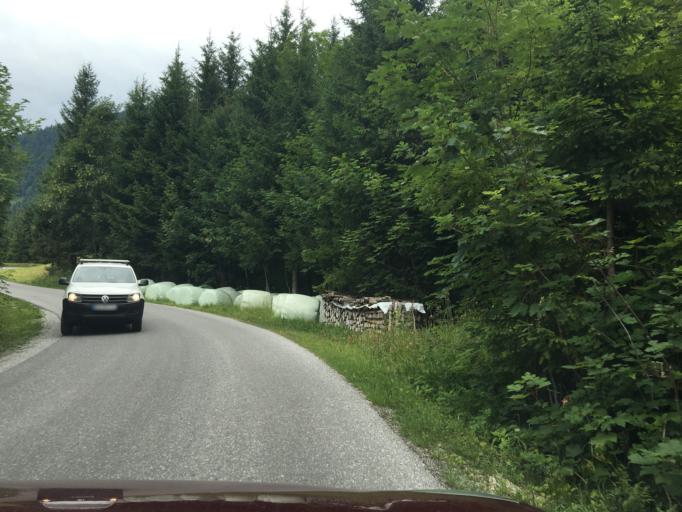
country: AT
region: Salzburg
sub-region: Politischer Bezirk Hallein
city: Abtenau
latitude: 47.6032
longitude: 13.3686
